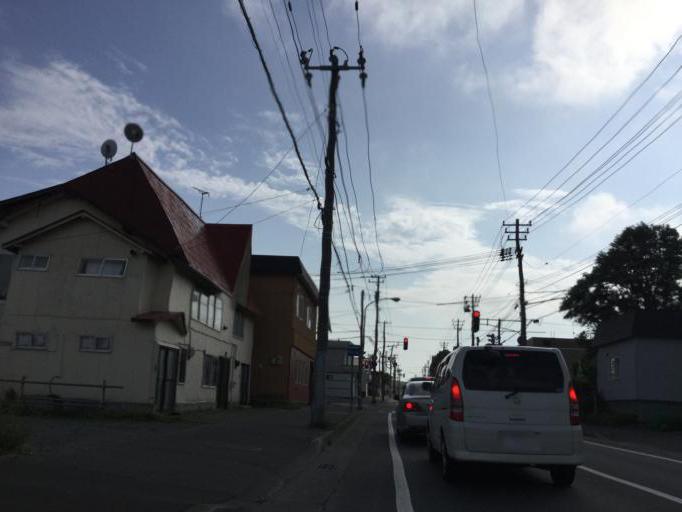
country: JP
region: Hokkaido
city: Wakkanai
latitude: 45.3908
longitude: 141.6804
